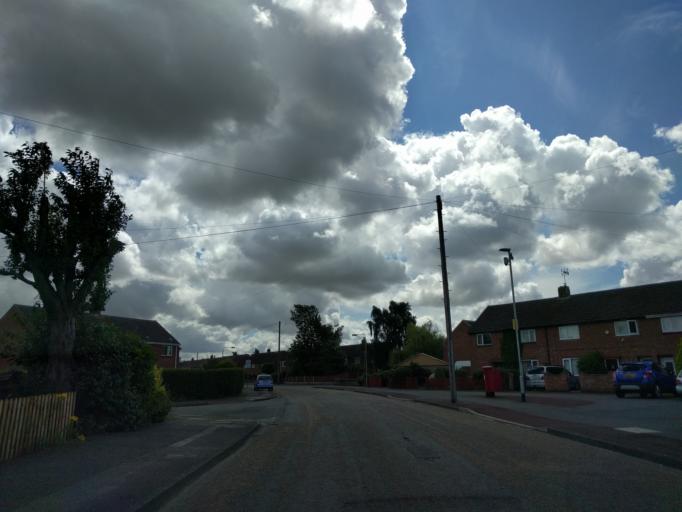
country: GB
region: England
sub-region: Nottinghamshire
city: Newark on Trent
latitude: 53.0595
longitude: -0.8110
